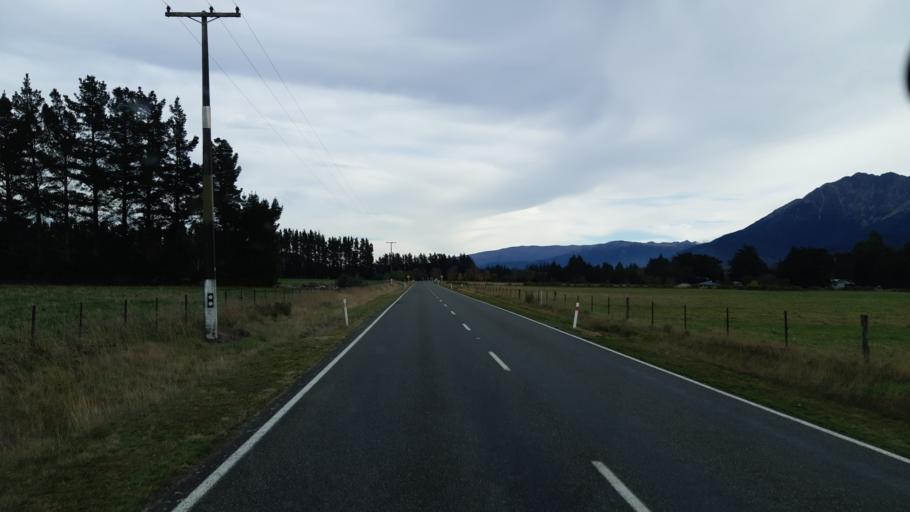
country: NZ
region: Tasman
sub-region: Tasman District
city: Brightwater
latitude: -41.6275
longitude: 173.3404
